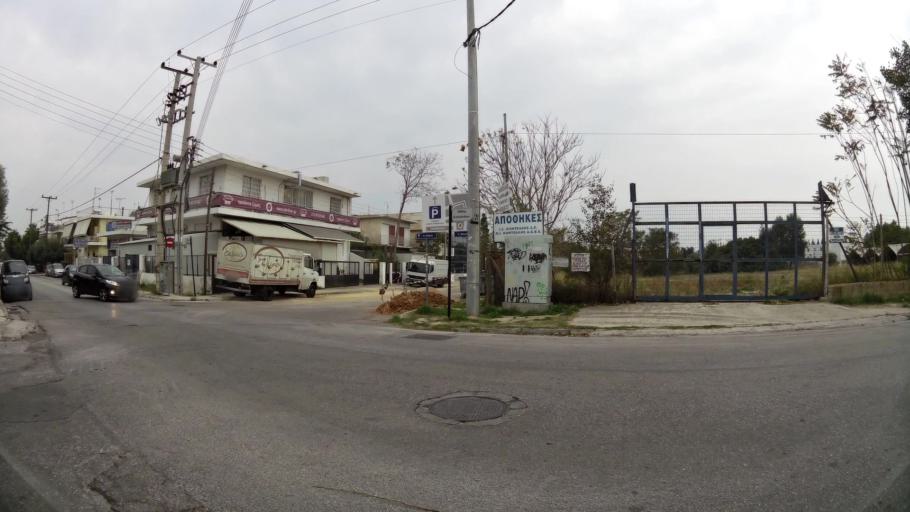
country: GR
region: Attica
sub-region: Nomarchia Athinas
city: Argyroupoli
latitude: 37.9141
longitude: 23.7425
